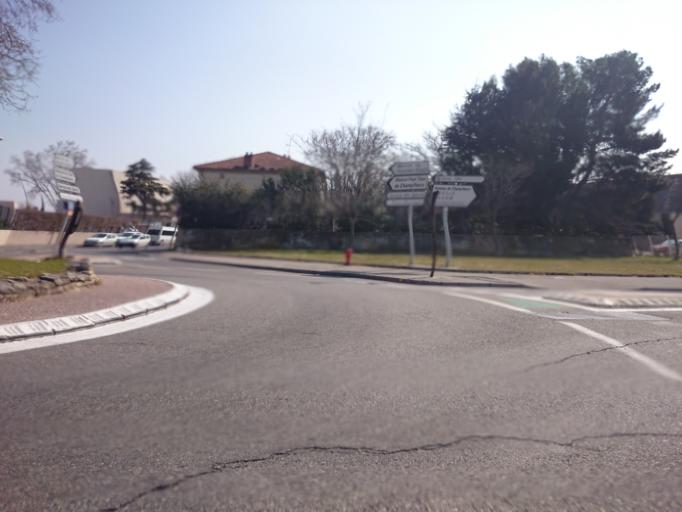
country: FR
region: Provence-Alpes-Cote d'Azur
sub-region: Departement du Vaucluse
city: Avignon
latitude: 43.9386
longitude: 4.7970
